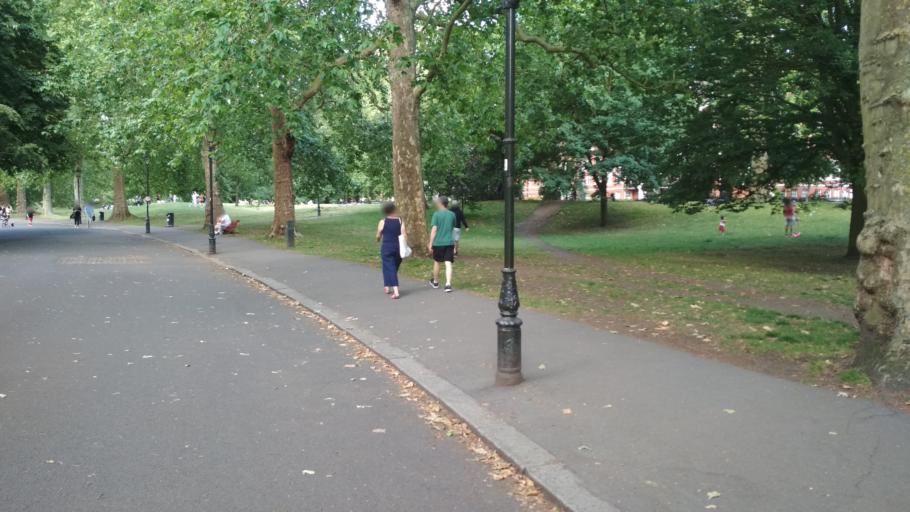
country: GB
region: England
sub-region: Greater London
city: Battersea
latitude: 51.4754
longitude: -0.1609
